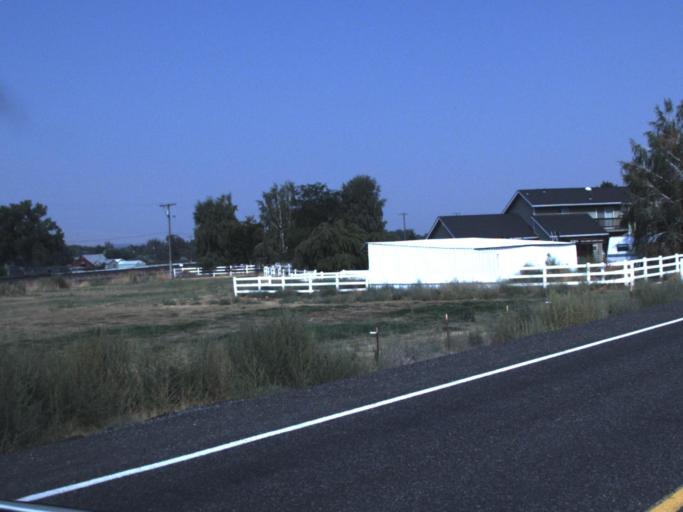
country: US
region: Washington
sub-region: Benton County
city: Prosser
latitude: 46.1931
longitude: -119.8054
